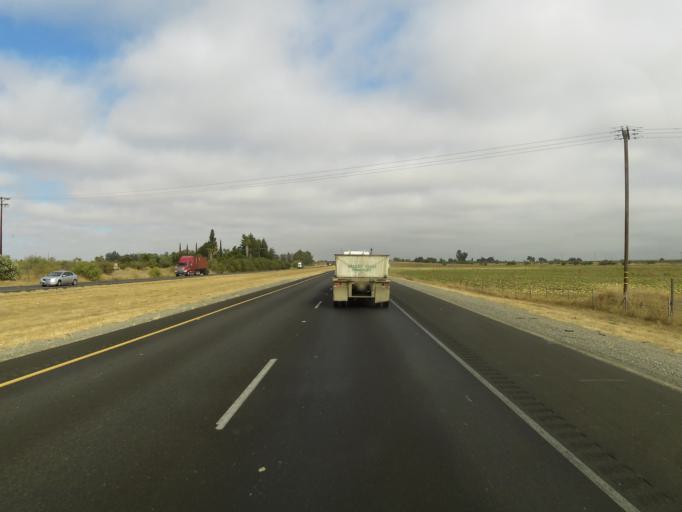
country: US
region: California
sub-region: Yolo County
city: Dunnigan
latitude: 38.9045
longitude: -121.9861
